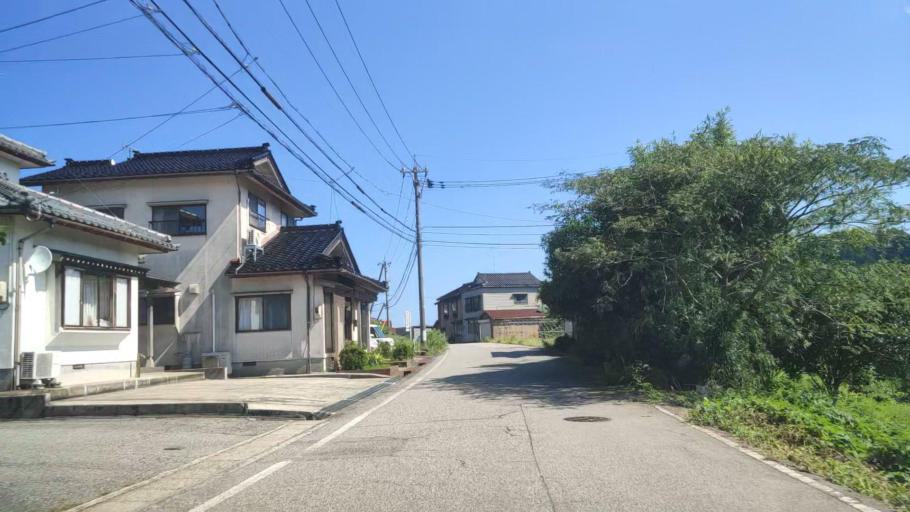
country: JP
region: Ishikawa
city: Nanao
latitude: 37.3724
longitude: 136.8737
